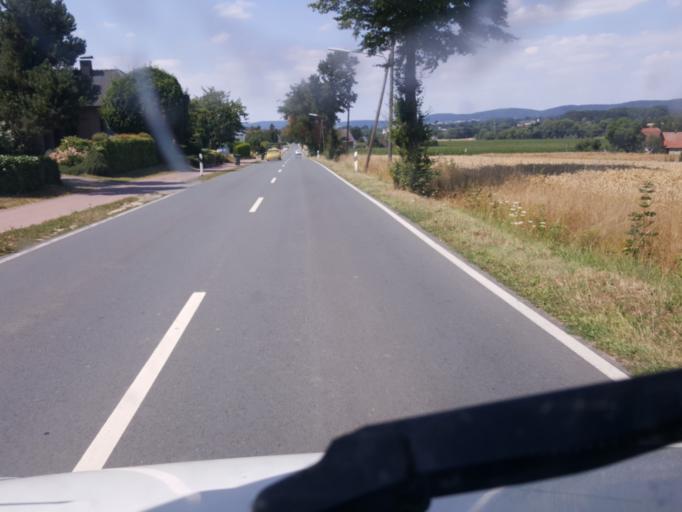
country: DE
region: North Rhine-Westphalia
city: Bad Oeynhausen
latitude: 52.2294
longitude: 8.7624
